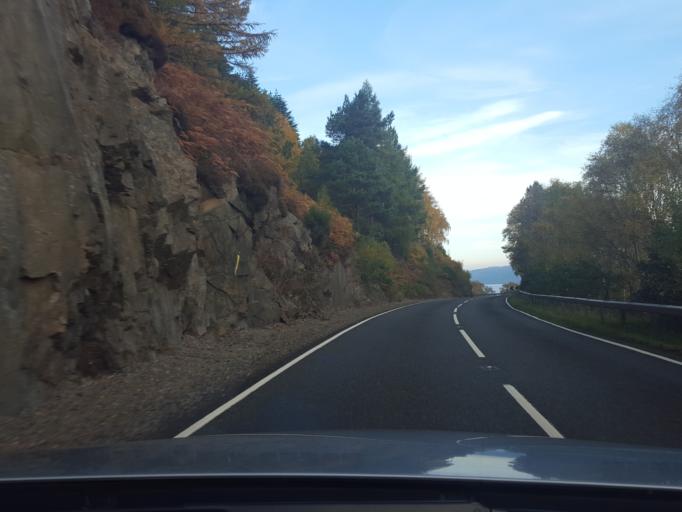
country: GB
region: Scotland
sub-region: Highland
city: Beauly
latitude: 57.3467
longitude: -4.4176
